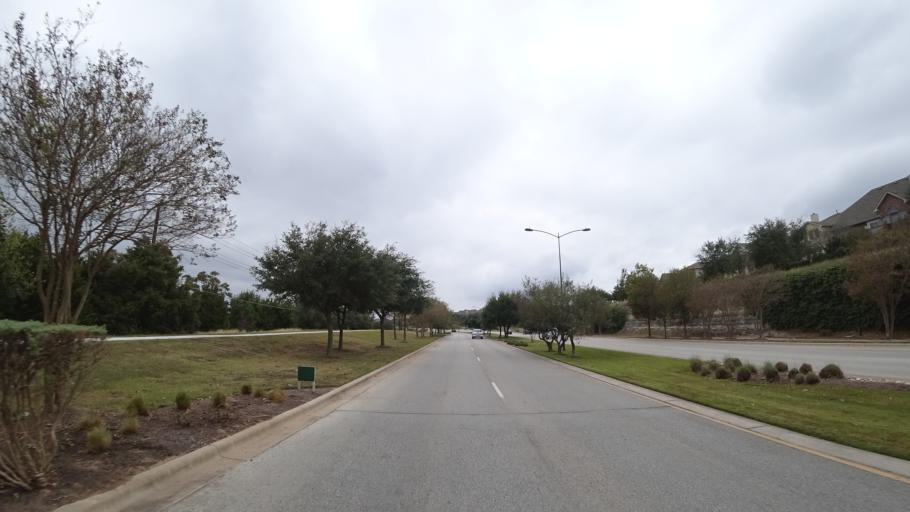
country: US
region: Texas
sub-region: Travis County
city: Hudson Bend
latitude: 30.3677
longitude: -97.8942
